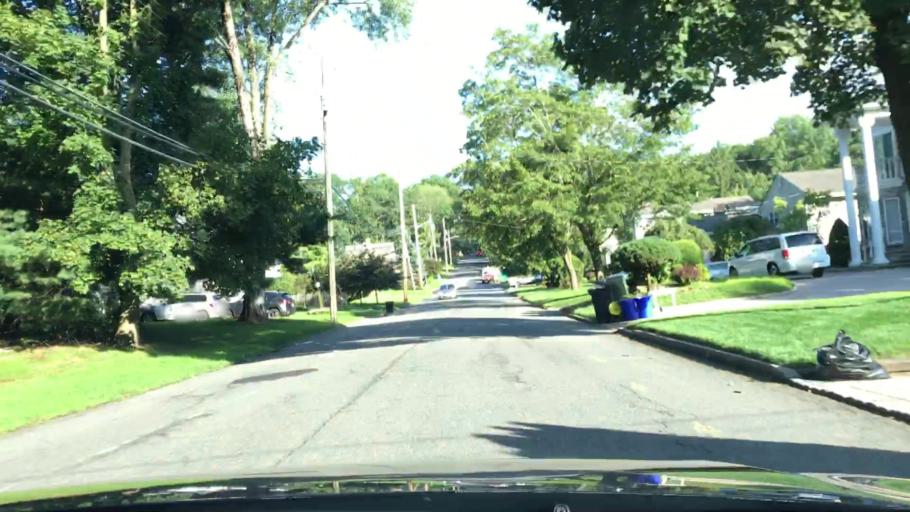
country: US
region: New Jersey
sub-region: Bergen County
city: Cresskill
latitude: 40.9373
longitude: -73.9552
